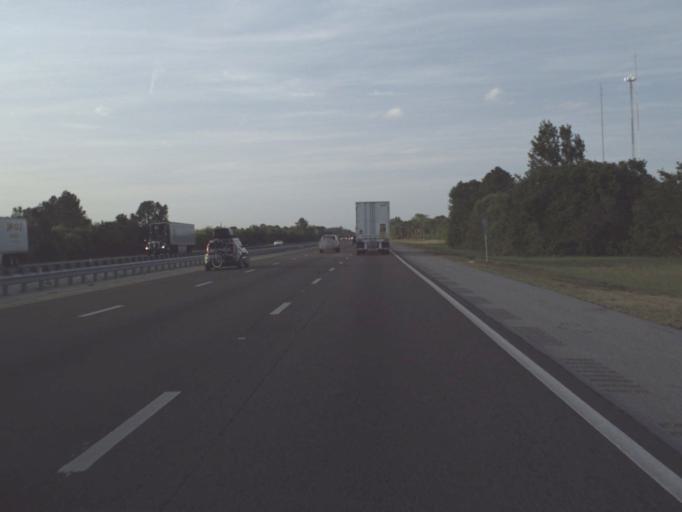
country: US
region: Florida
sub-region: Brevard County
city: Titusville
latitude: 28.5755
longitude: -80.8513
